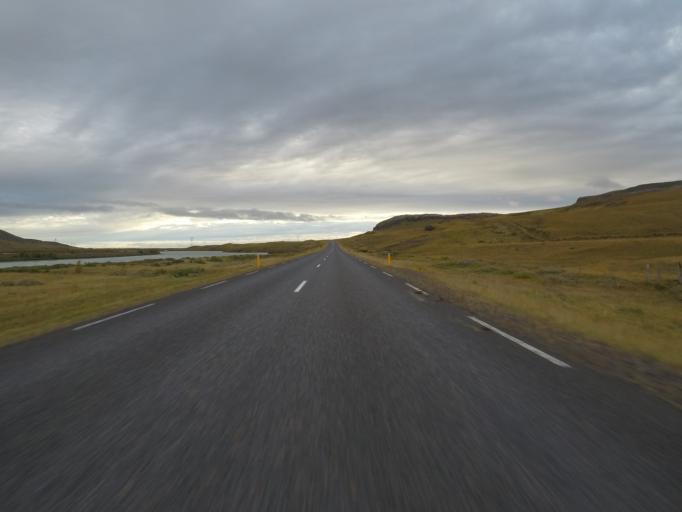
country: IS
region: South
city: Vestmannaeyjar
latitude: 64.0571
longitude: -20.1262
